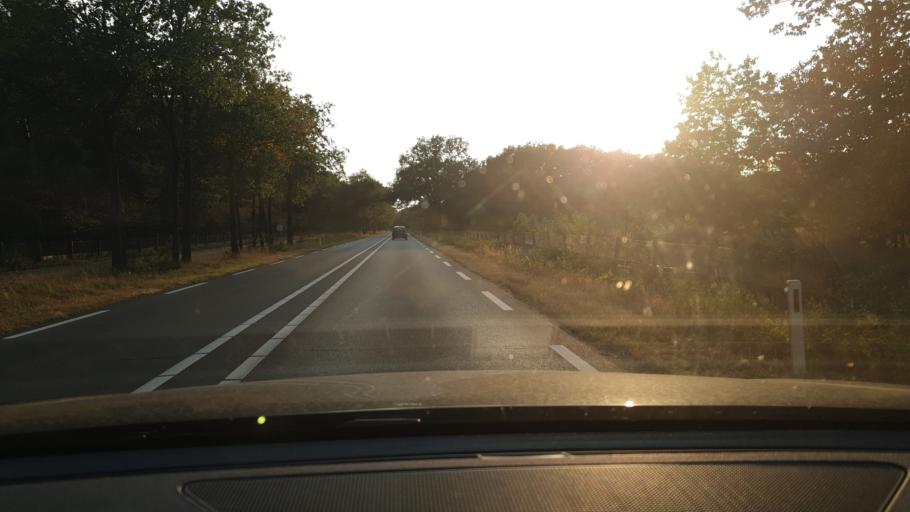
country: NL
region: North Brabant
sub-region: Gemeente Mill en Sint Hubert
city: Wilbertoord
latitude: 51.6735
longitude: 5.7921
